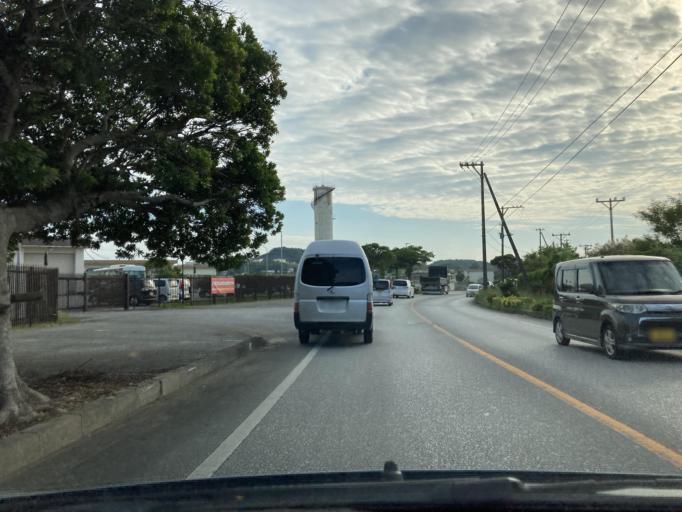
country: JP
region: Okinawa
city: Okinawa
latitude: 26.3653
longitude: 127.7976
